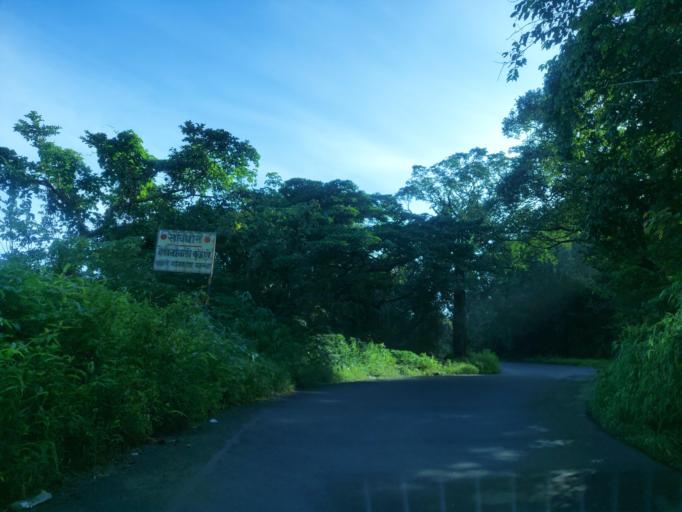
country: IN
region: Maharashtra
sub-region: Sindhudurg
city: Savantvadi
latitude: 15.9371
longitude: 73.9703
